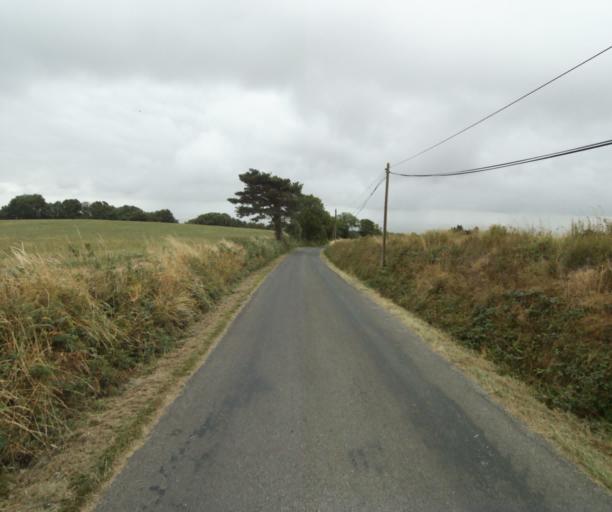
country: FR
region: Midi-Pyrenees
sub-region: Departement du Tarn
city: Soreze
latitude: 43.4034
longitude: 2.0643
